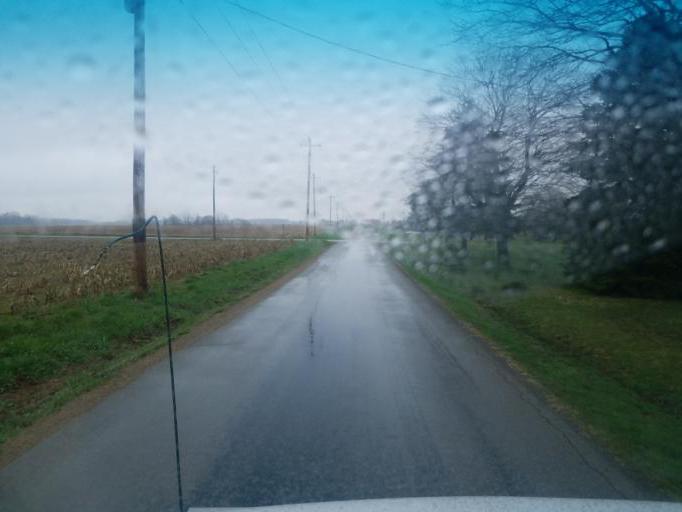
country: US
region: Ohio
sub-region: Seneca County
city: Tiffin
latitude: 40.9644
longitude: -83.1327
